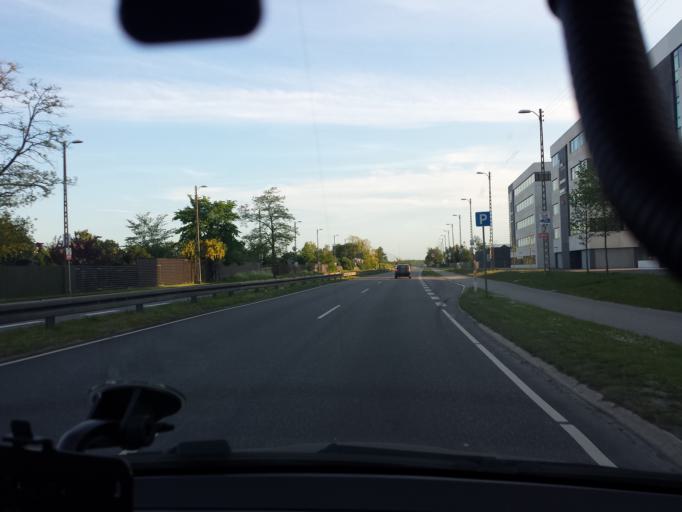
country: DK
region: Capital Region
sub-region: Herlev Kommune
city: Herlev
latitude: 55.7154
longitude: 12.4374
